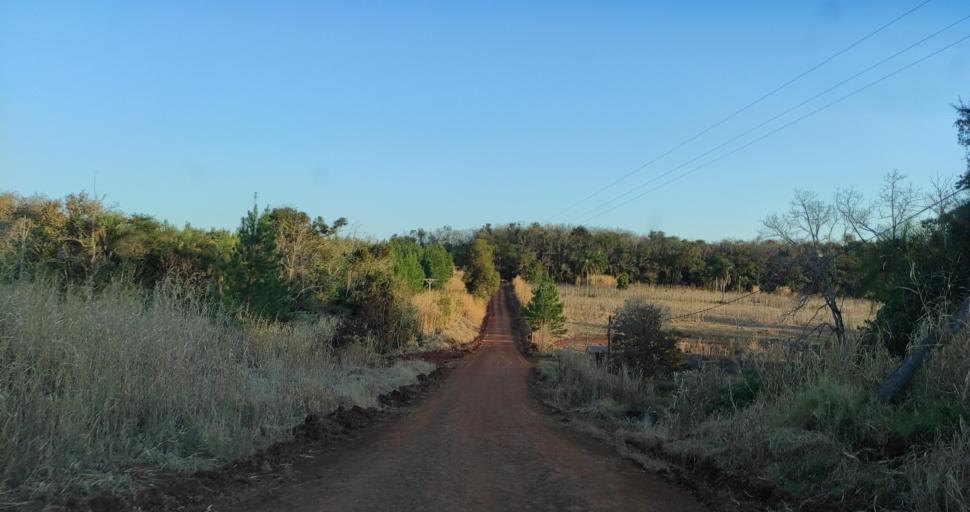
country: AR
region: Misiones
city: Capiovi
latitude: -26.8789
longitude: -55.1228
